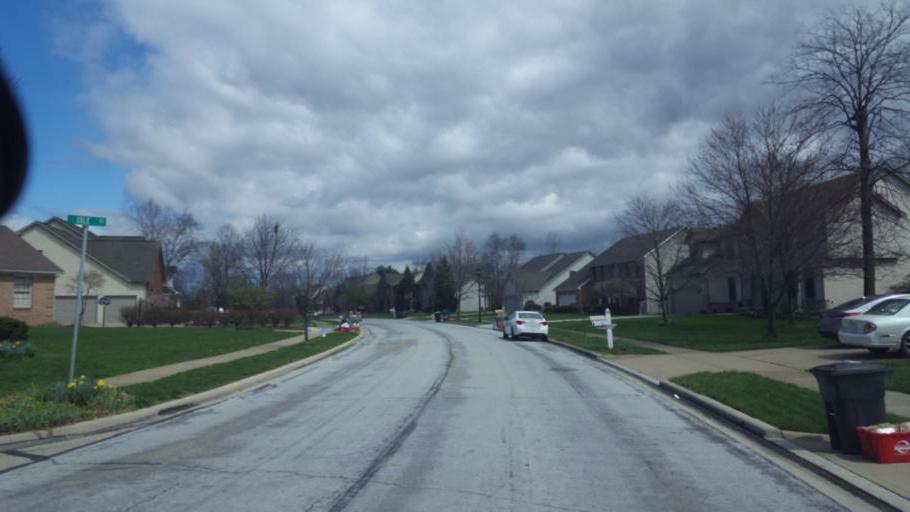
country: US
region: Ohio
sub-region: Franklin County
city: Westerville
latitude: 40.1428
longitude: -82.8905
